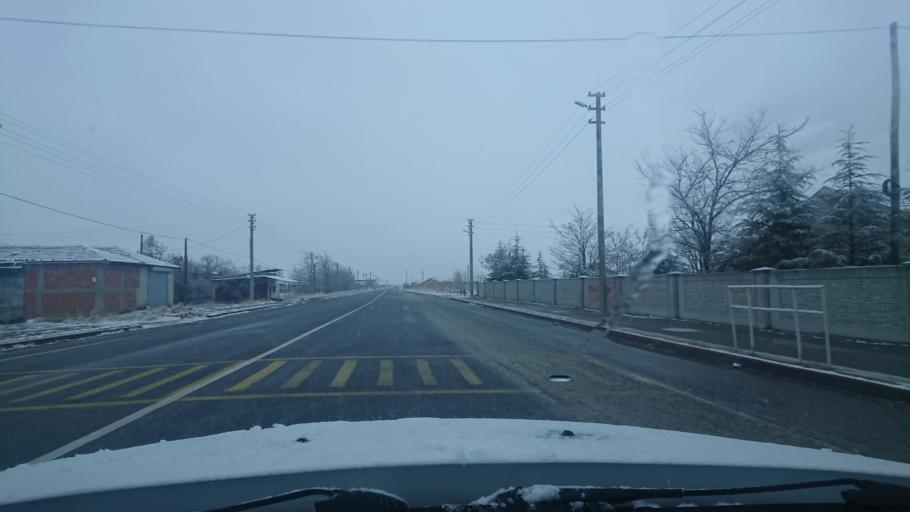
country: TR
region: Aksaray
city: Yesilova
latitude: 38.2921
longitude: 33.7601
